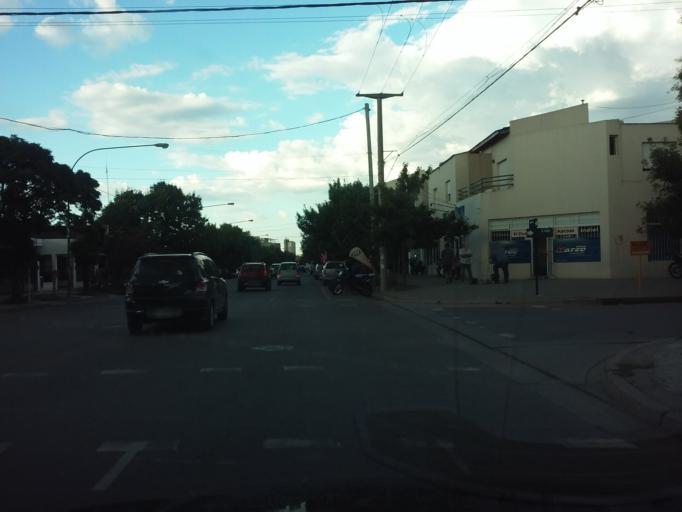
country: AR
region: La Pampa
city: Santa Rosa
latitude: -36.6286
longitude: -64.2915
